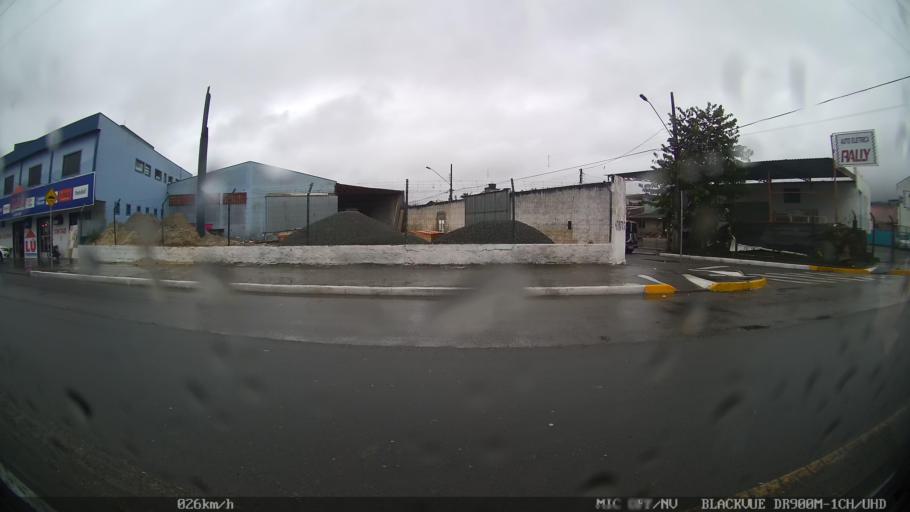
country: BR
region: Santa Catarina
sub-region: Itajai
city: Itajai
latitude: -26.9249
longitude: -48.6955
